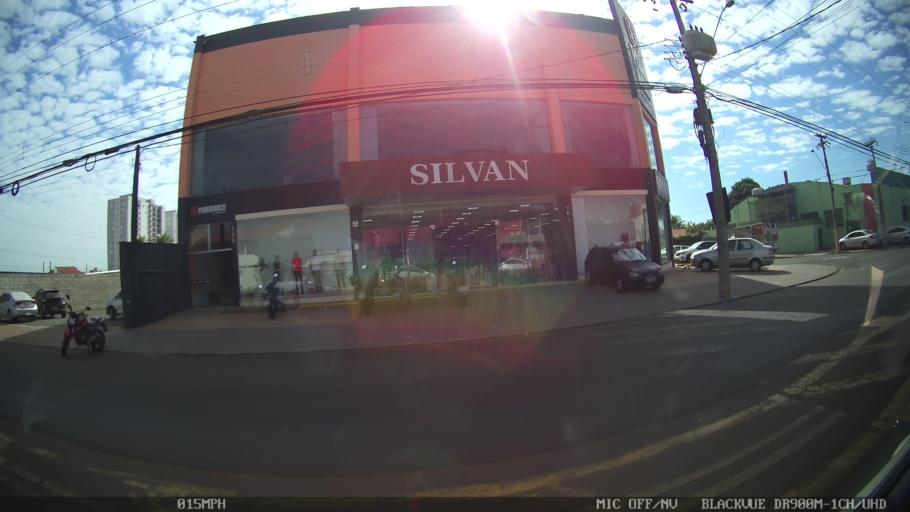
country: BR
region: Sao Paulo
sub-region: Santa Barbara D'Oeste
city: Santa Barbara d'Oeste
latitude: -22.7615
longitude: -47.3968
